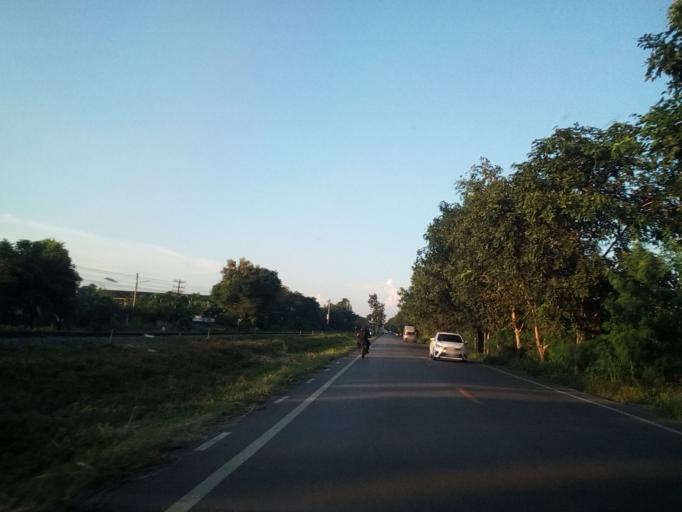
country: TH
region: Lamphun
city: Lamphun
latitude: 18.6319
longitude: 99.0408
